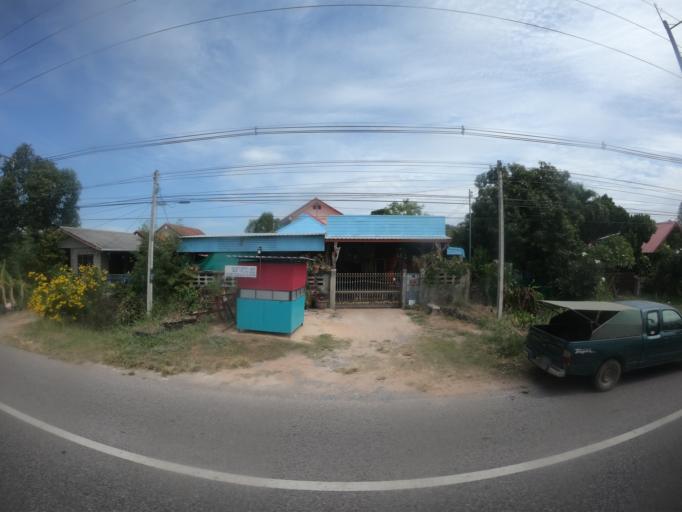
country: TH
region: Maha Sarakham
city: Chiang Yuen
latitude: 16.4233
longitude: 103.0715
